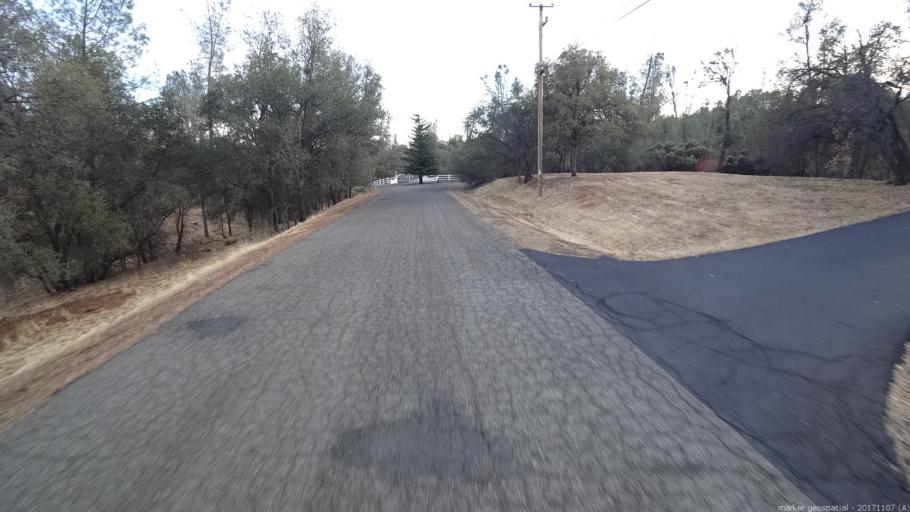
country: US
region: California
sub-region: Shasta County
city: Shasta
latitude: 40.5341
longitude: -122.4808
